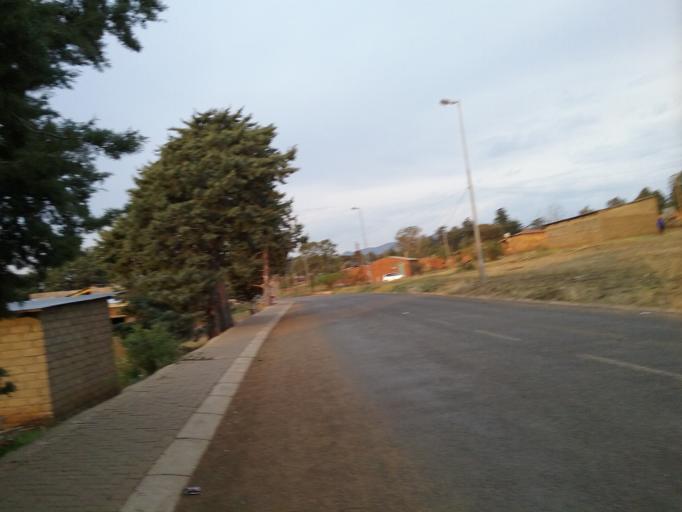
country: LS
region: Quthing
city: Quthing
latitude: -30.4075
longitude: 27.7029
